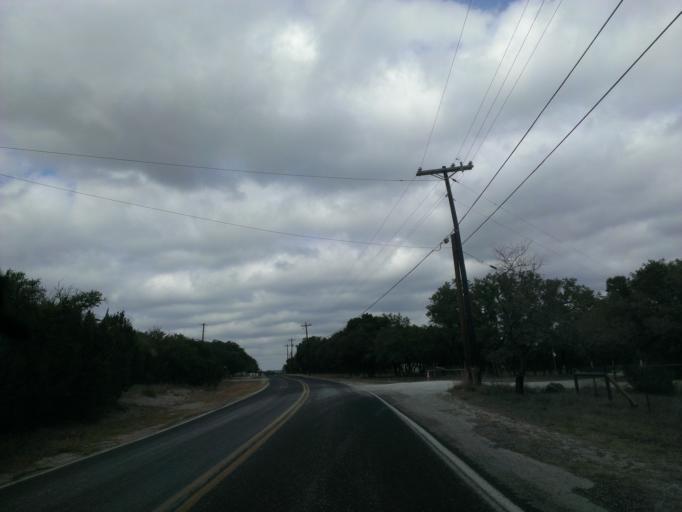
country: US
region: Texas
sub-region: Travis County
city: Briarcliff
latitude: 30.3817
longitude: -98.0952
